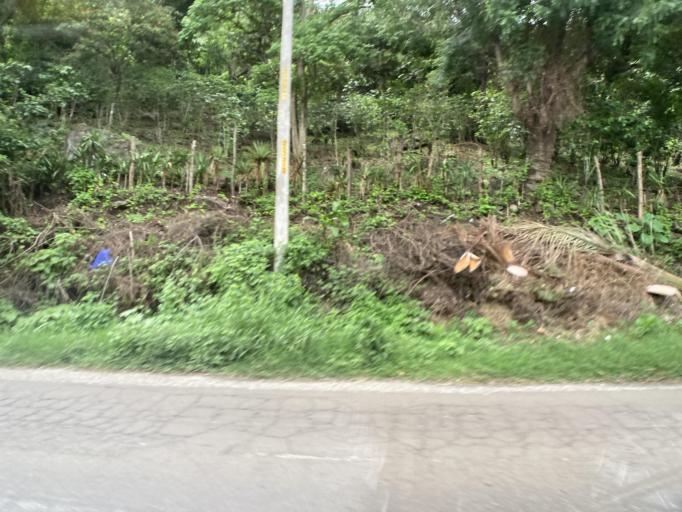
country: GT
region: Guatemala
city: Villa Canales
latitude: 14.4233
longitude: -90.5346
